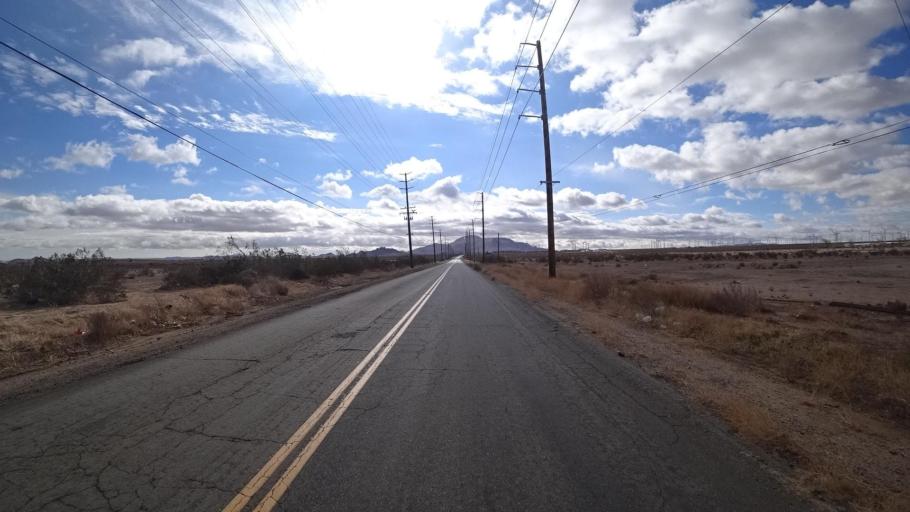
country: US
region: California
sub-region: Kern County
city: Mojave
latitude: 35.0497
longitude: -118.1855
